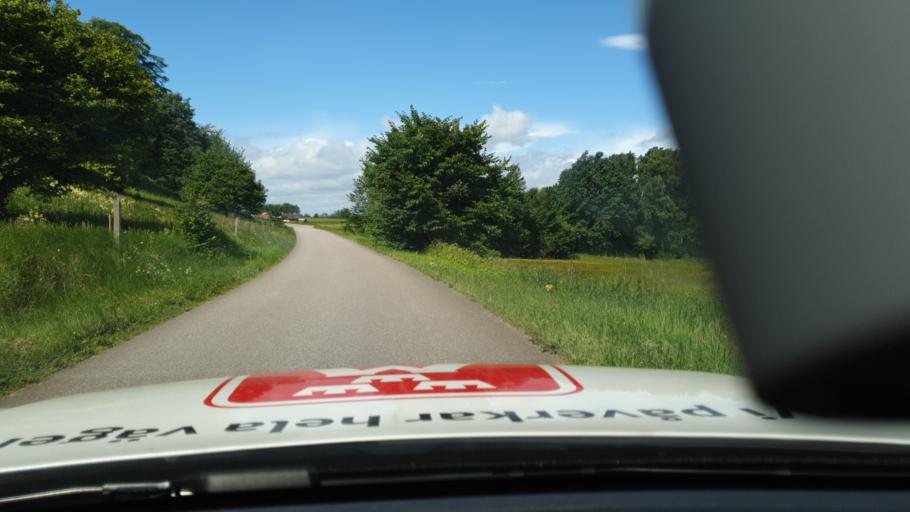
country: SE
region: Vaestra Goetaland
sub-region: Falkopings Kommun
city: Falkoeping
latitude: 58.1437
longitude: 13.6067
